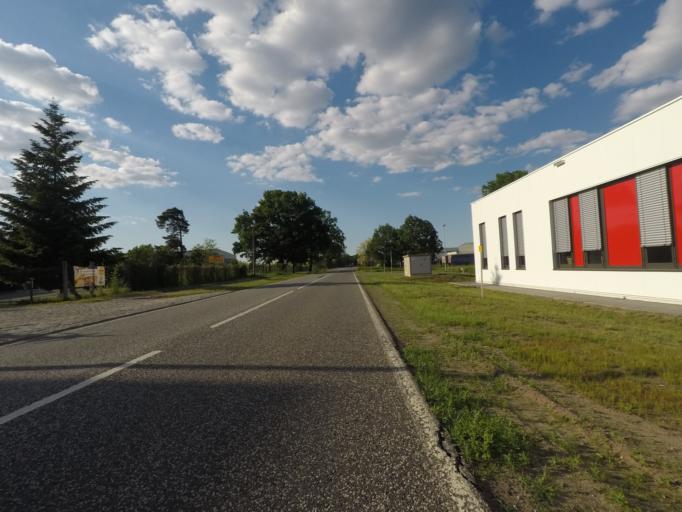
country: DE
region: Brandenburg
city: Eberswalde
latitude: 52.8492
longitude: 13.7902
